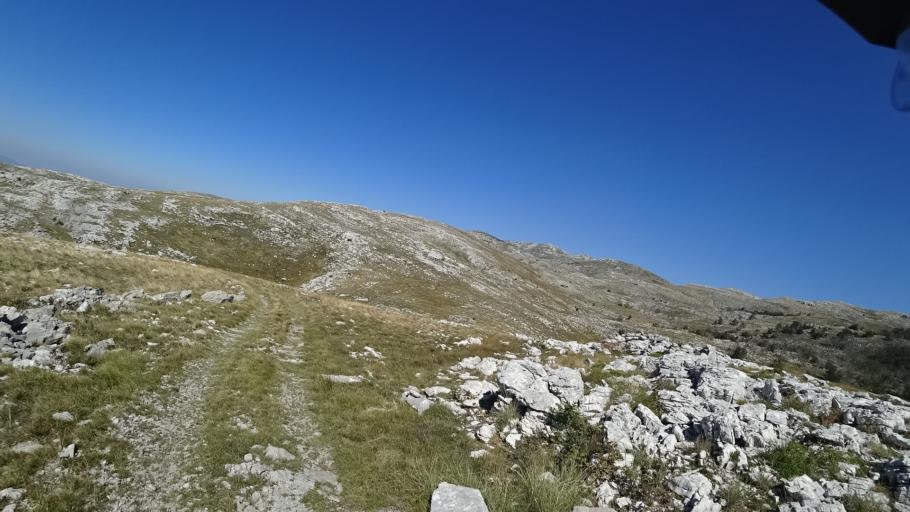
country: HR
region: Splitsko-Dalmatinska
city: Hrvace
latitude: 43.9163
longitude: 16.6060
